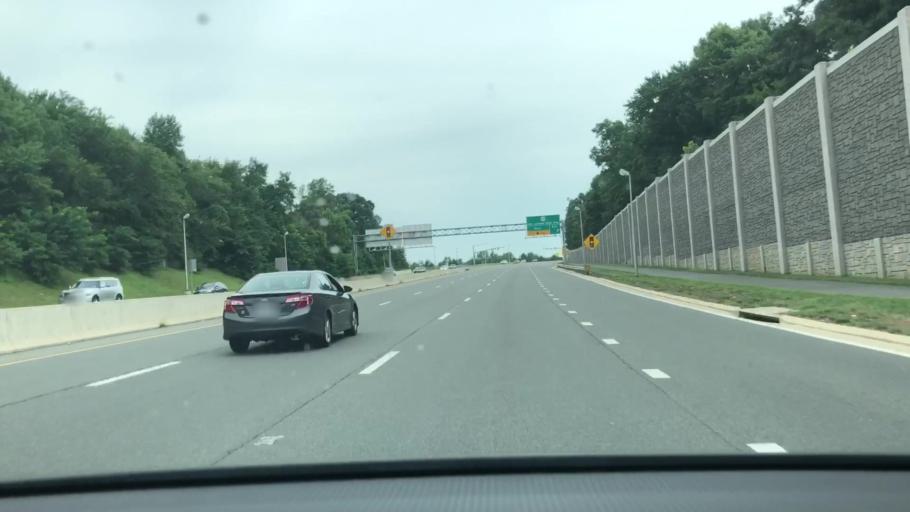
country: US
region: Virginia
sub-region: Fairfax County
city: Greenbriar
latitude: 38.8710
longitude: -77.3835
